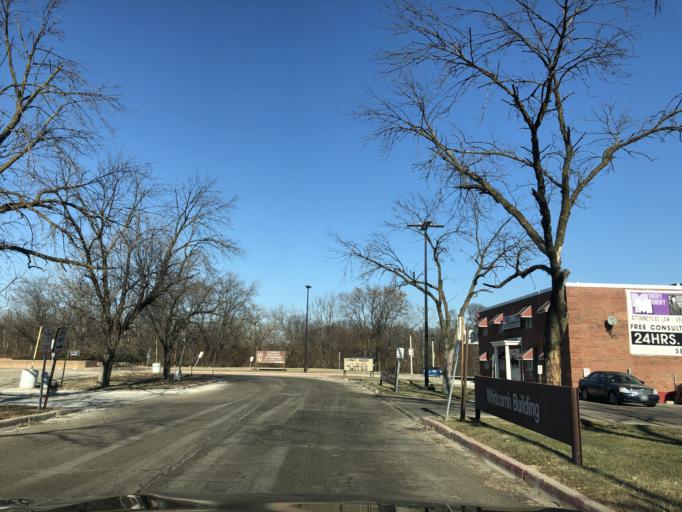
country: US
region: Illinois
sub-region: Cook County
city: Forest Park
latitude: 41.8746
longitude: -87.8263
